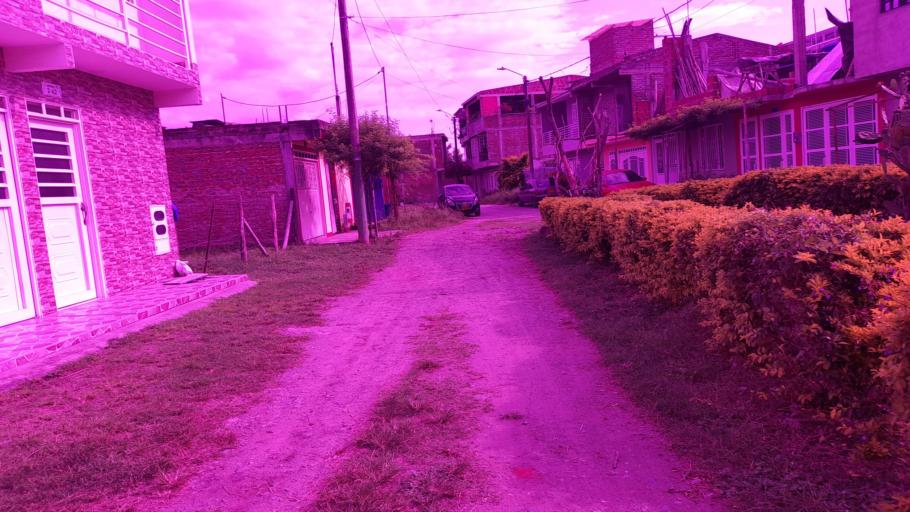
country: CO
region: Valle del Cauca
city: Guacari
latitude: 3.7600
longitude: -76.3238
